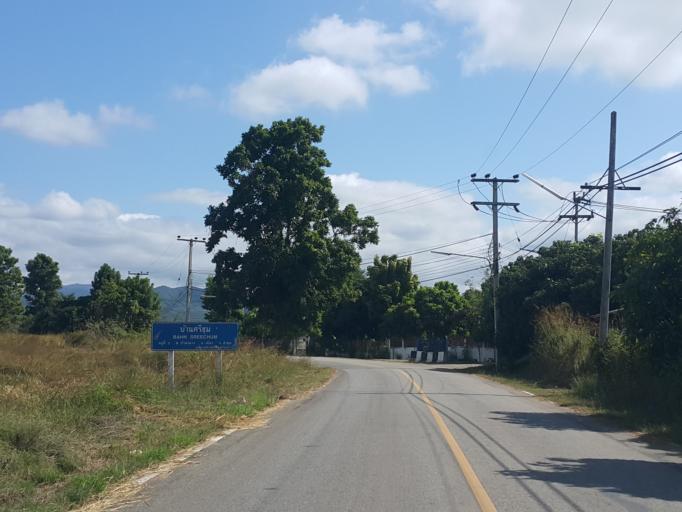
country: TH
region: Lamphun
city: Ban Thi
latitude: 18.5702
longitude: 99.0857
